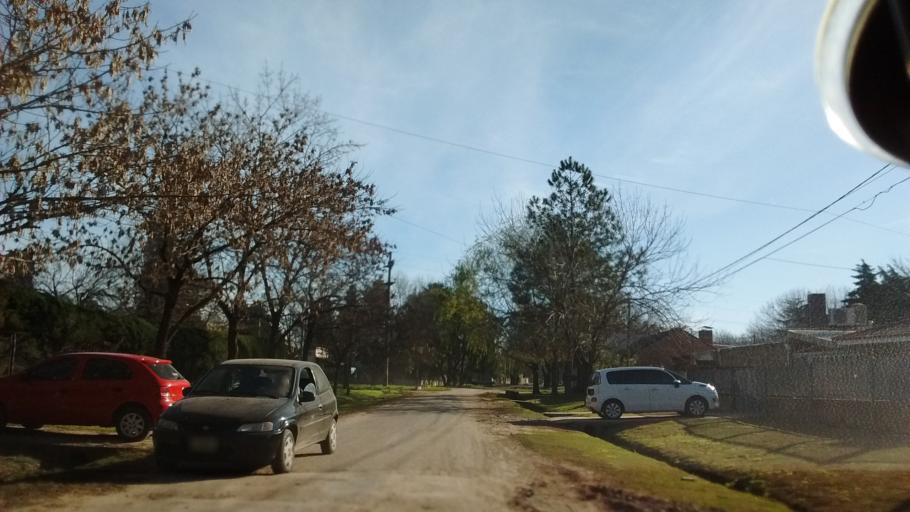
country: AR
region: Santa Fe
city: Funes
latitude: -32.9261
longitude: -60.8081
